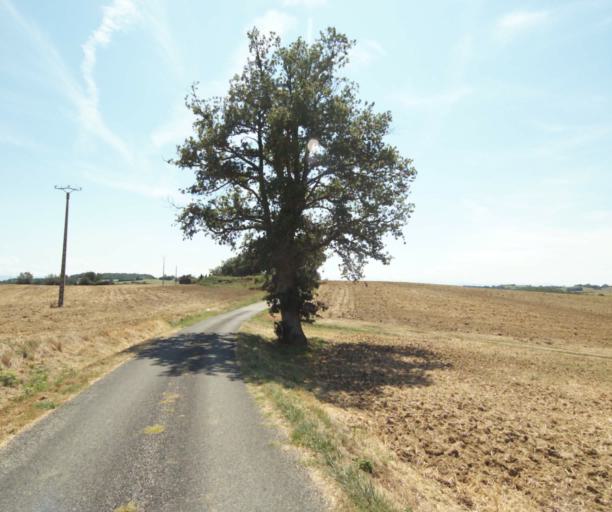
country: FR
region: Midi-Pyrenees
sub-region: Departement de l'Ariege
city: Lezat-sur-Leze
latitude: 43.2486
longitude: 1.3284
